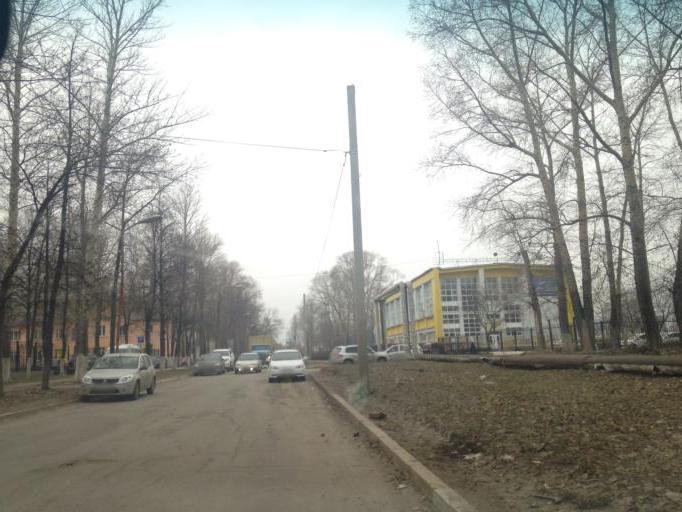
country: RU
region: Ulyanovsk
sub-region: Ulyanovskiy Rayon
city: Ulyanovsk
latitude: 54.2934
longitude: 48.2968
